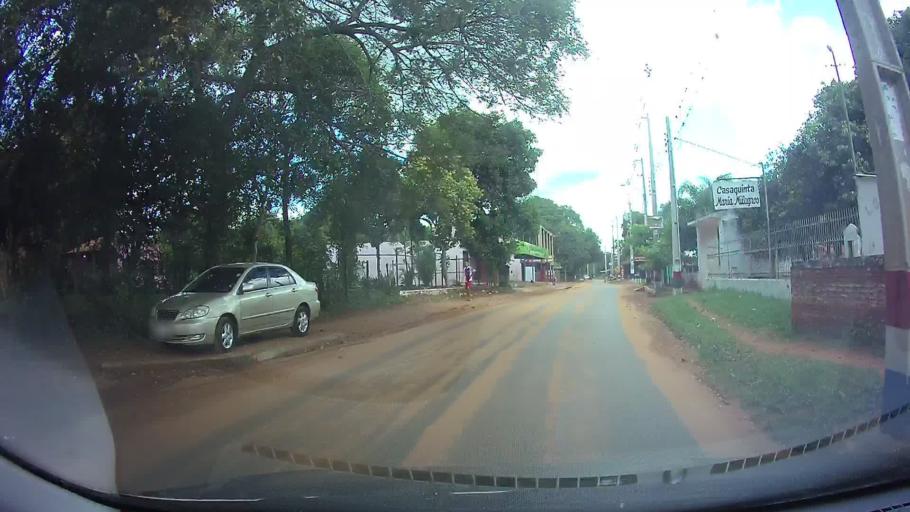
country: PY
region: Central
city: Capiata
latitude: -25.3337
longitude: -57.4201
